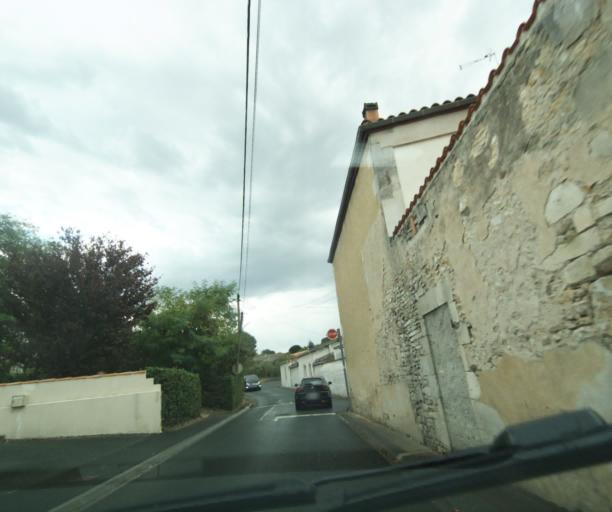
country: FR
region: Poitou-Charentes
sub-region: Departement de la Charente-Maritime
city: Tonnay-Charente
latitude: 45.9447
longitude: -0.8895
